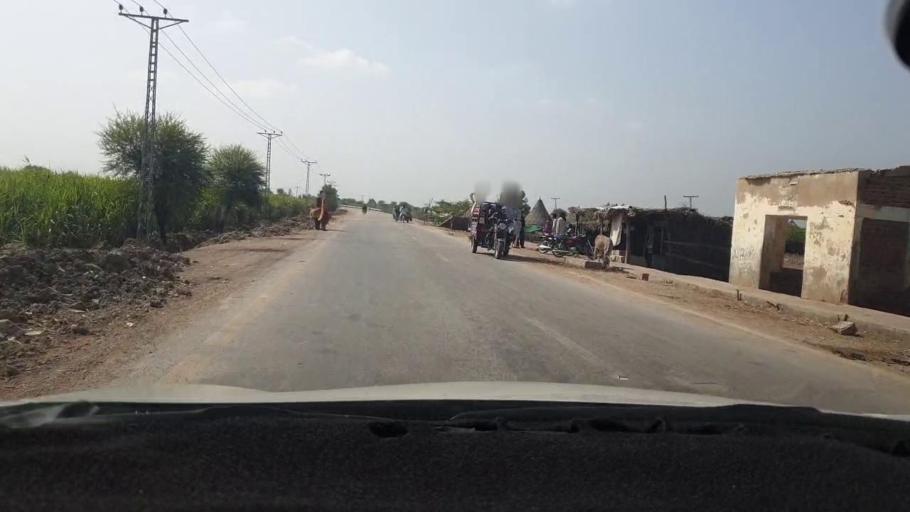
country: PK
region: Sindh
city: Mirpur Khas
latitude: 25.7701
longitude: 69.0713
